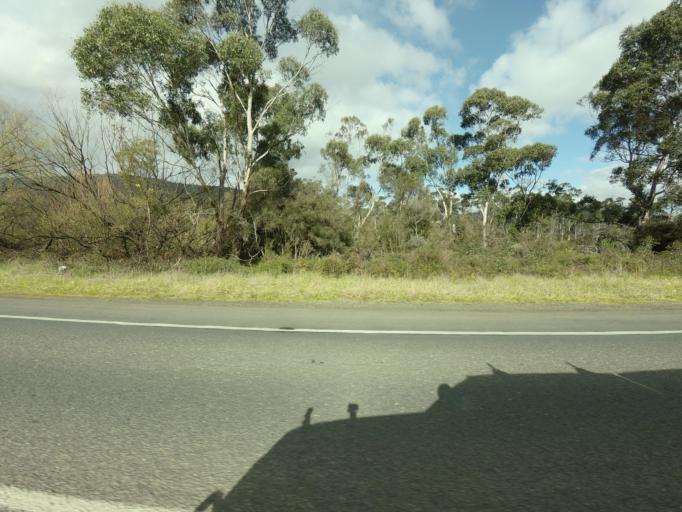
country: AU
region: Tasmania
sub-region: Huon Valley
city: Huonville
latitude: -43.0572
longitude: 147.0305
